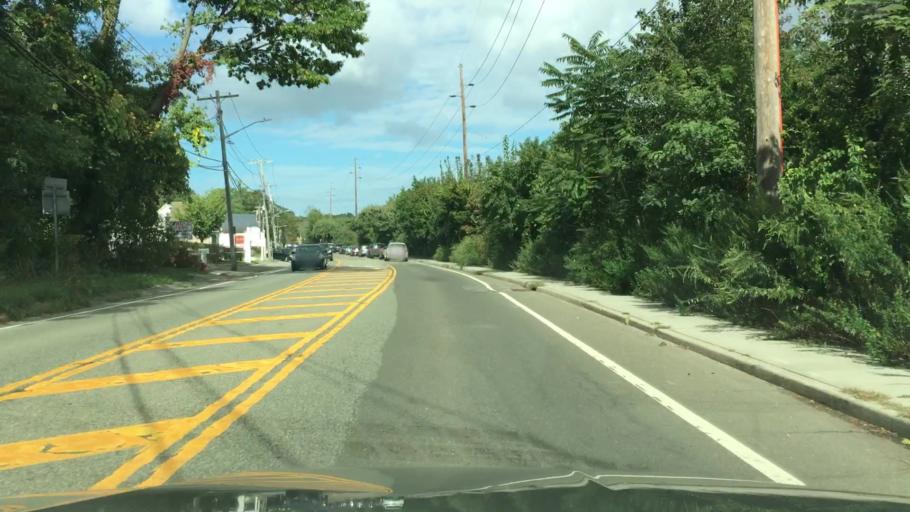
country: US
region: New York
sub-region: Suffolk County
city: Stony Brook
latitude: 40.9186
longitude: -73.1300
